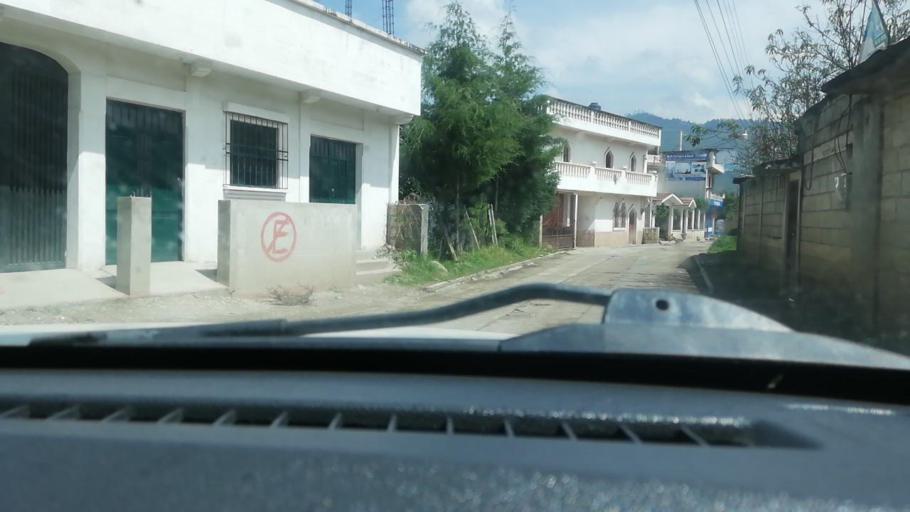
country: GT
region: Totonicapan
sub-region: Municipio de San Andres Xecul
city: San Andres Xecul
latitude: 14.8895
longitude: -91.4732
